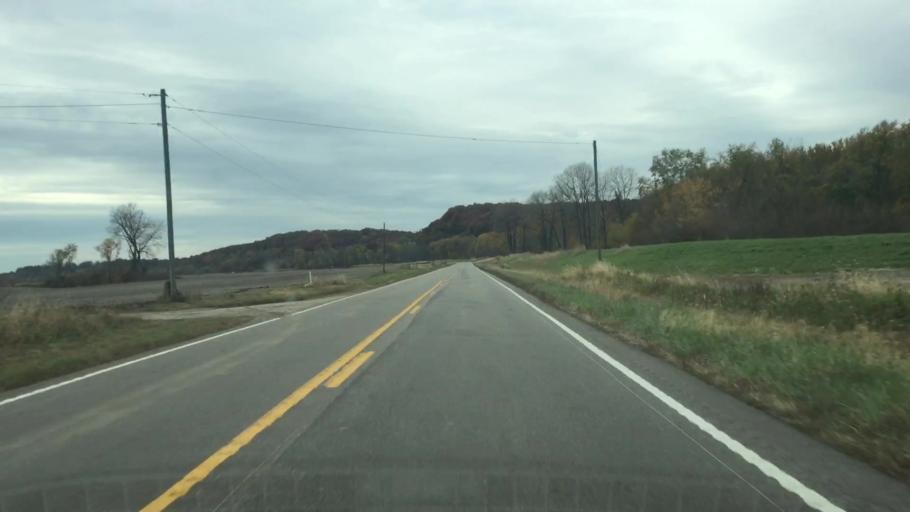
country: US
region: Missouri
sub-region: Callaway County
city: Fulton
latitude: 38.7056
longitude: -91.7773
